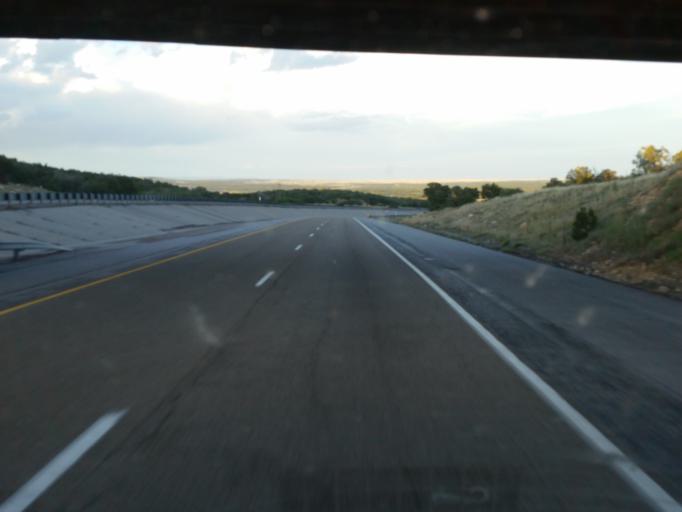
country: US
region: New Mexico
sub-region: Torrance County
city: Moriarty
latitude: 35.0037
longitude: -105.5464
